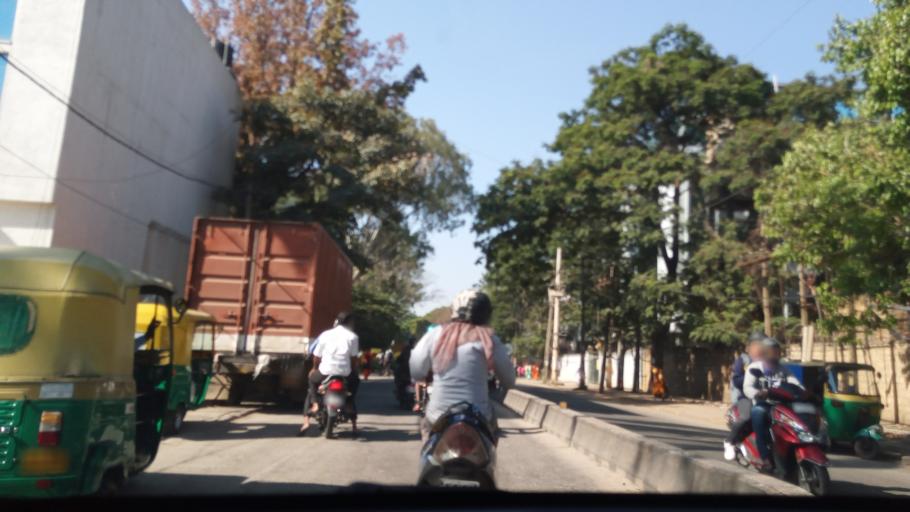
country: IN
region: Karnataka
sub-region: Bangalore Urban
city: Bangalore
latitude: 13.0257
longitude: 77.5438
